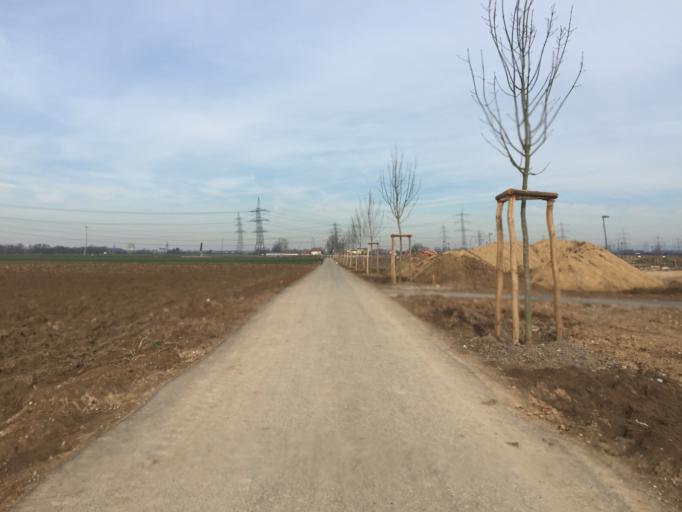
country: DE
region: Baden-Wuerttemberg
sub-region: Karlsruhe Region
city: Heddesheim
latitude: 49.5117
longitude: 8.6023
